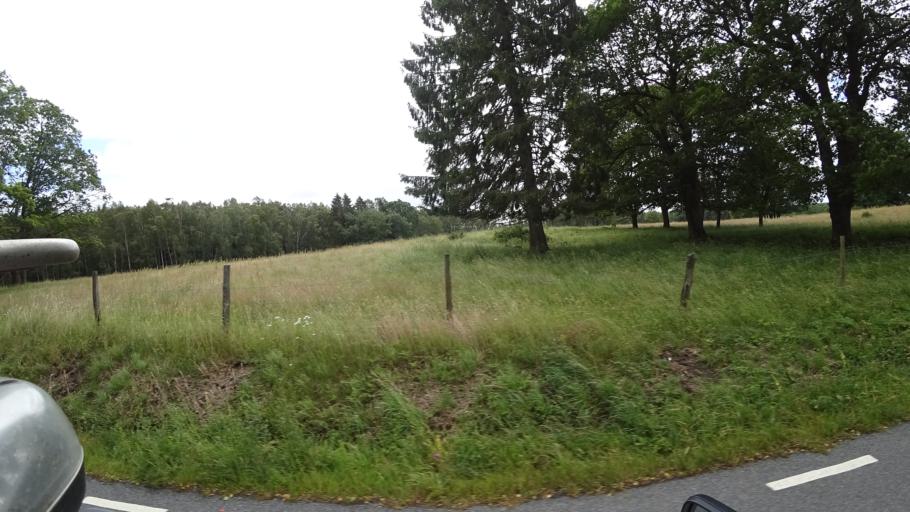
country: SE
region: Skane
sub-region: Kristianstads Kommun
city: Degeberga
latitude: 55.7163
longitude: 13.9885
